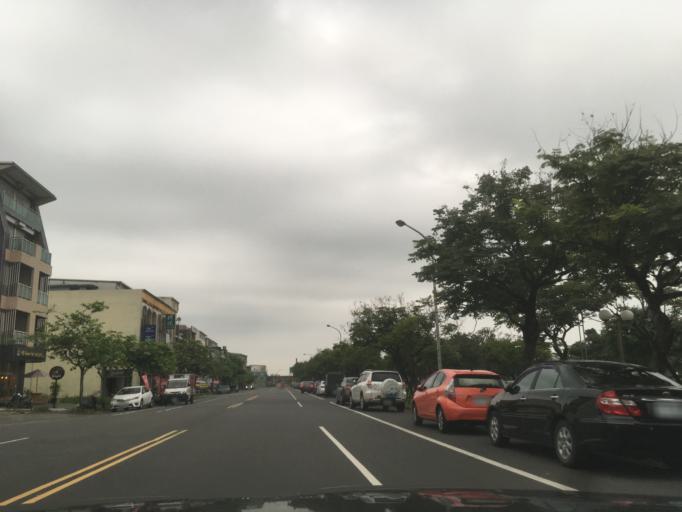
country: TW
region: Taiwan
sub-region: Yilan
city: Yilan
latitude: 24.7406
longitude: 121.7547
